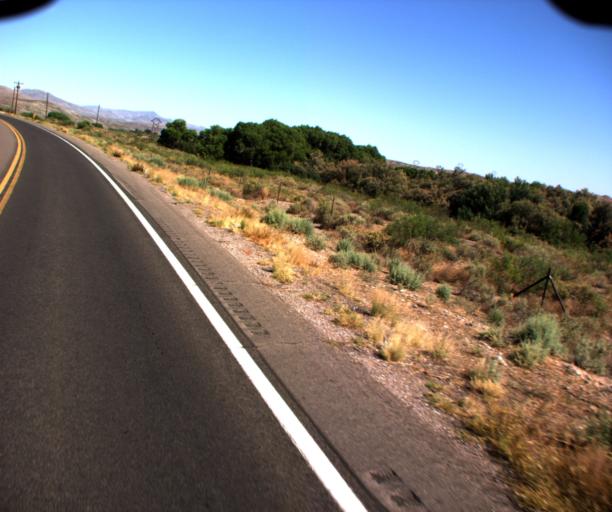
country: US
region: Arizona
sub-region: Greenlee County
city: Clifton
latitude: 32.7410
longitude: -109.1277
